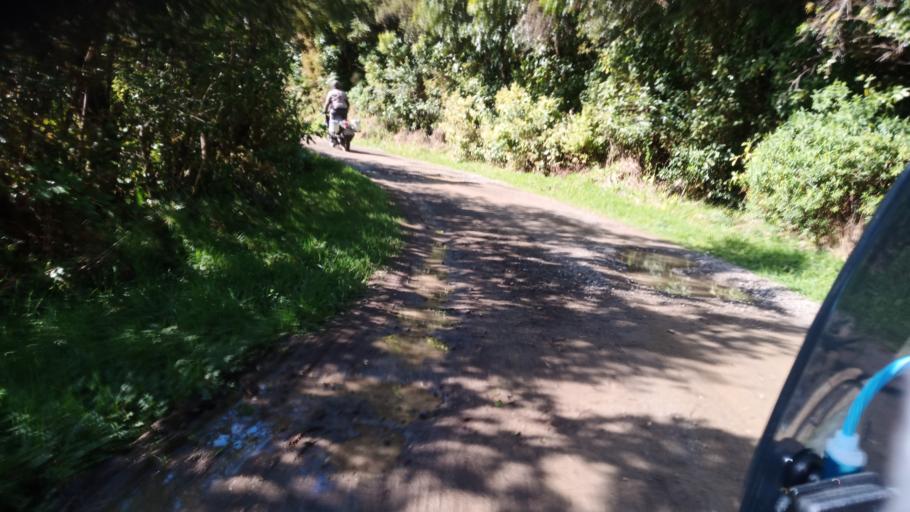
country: NZ
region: Hawke's Bay
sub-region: Wairoa District
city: Wairoa
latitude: -38.8008
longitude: 177.1159
